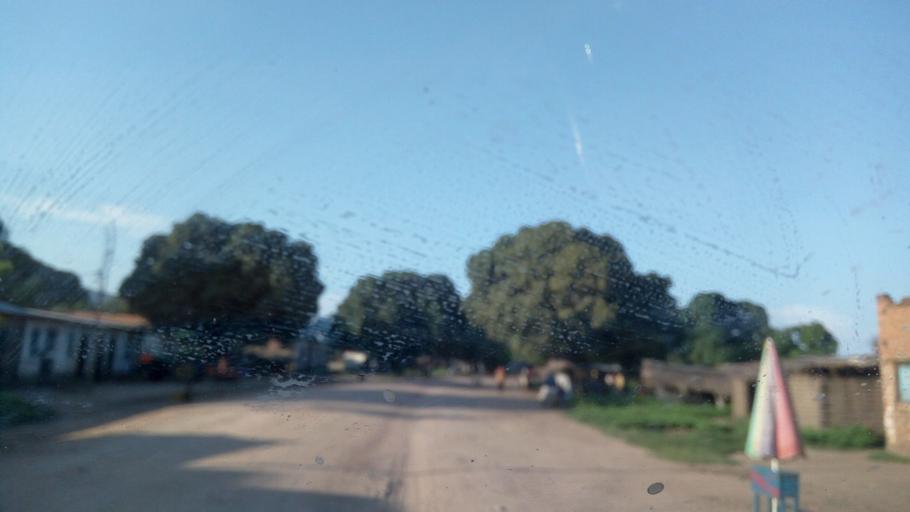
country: BI
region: Bururi
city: Rumonge
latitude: -4.1908
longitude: 29.0512
